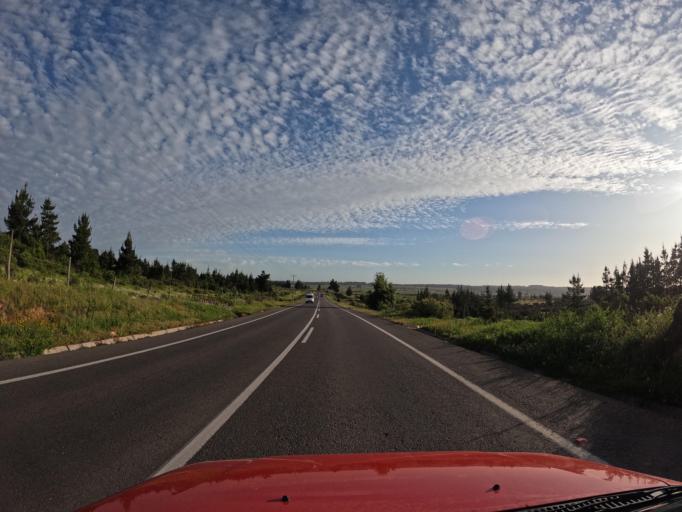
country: CL
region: Valparaiso
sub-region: San Antonio Province
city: San Antonio
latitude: -34.0523
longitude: -71.6239
